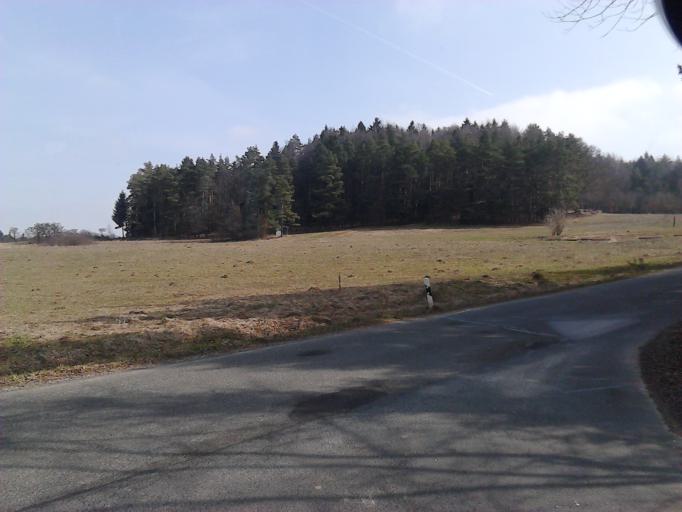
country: DE
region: Bavaria
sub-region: Upper Franconia
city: Obertrubach
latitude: 49.7231
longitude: 11.3510
